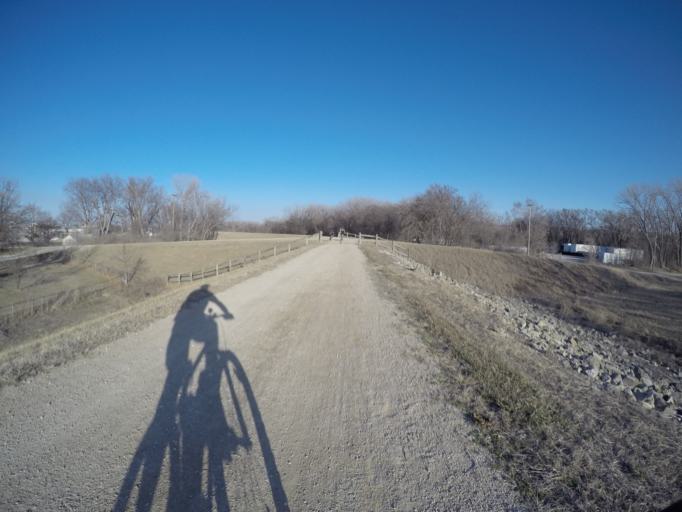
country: US
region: Kansas
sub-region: Riley County
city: Manhattan
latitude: 39.1707
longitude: -96.5637
